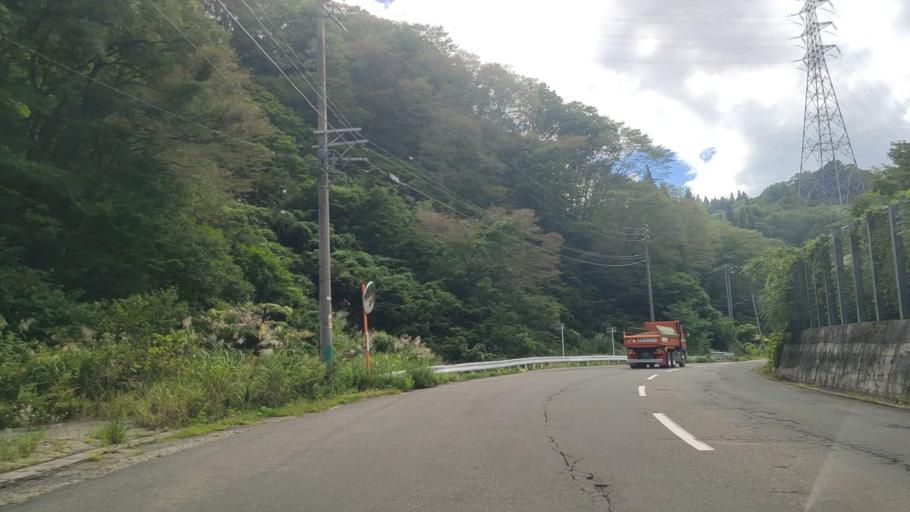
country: JP
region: Nagano
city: Iiyama
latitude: 36.8916
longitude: 138.3233
